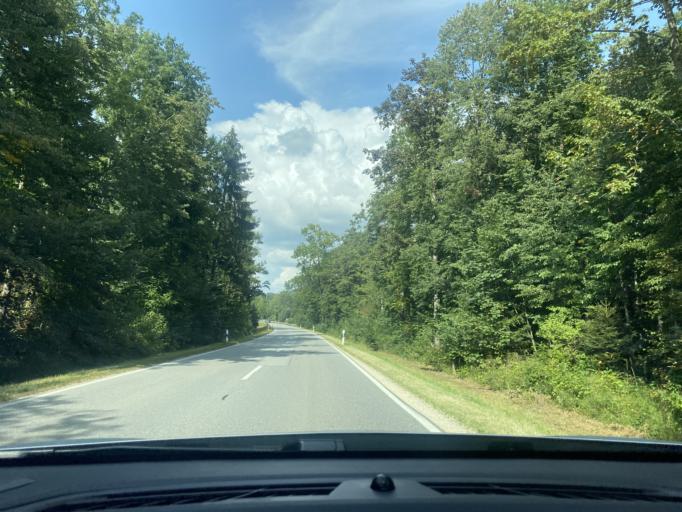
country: DE
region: Bavaria
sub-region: Upper Bavaria
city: Langenbach
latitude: 48.4521
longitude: 11.8524
